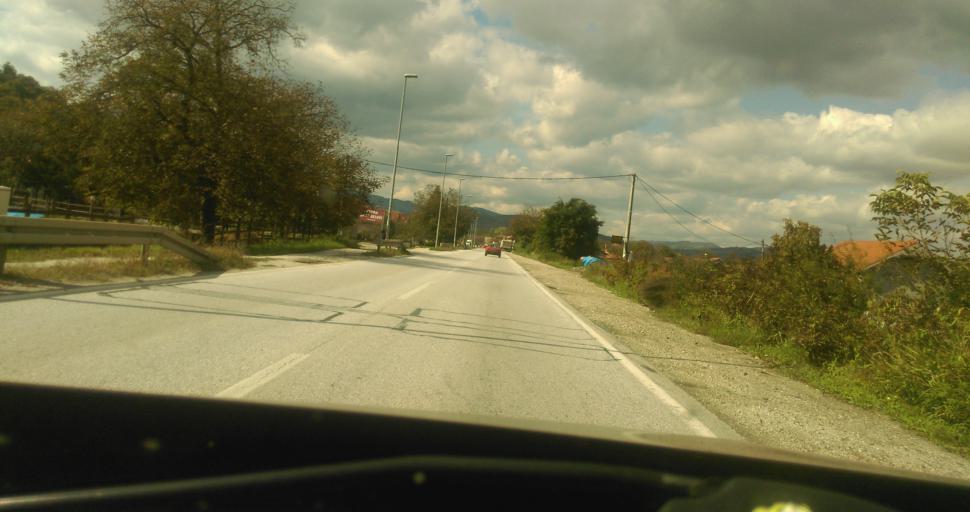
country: RS
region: Central Serbia
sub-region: Moravicki Okrug
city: Cacak
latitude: 43.8944
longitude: 20.3009
